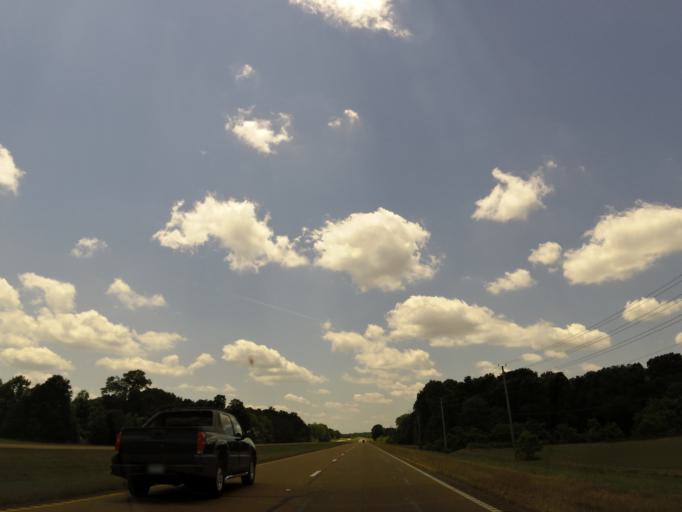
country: US
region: Mississippi
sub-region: Pontotoc County
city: Pontotoc
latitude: 34.2844
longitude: -89.0415
